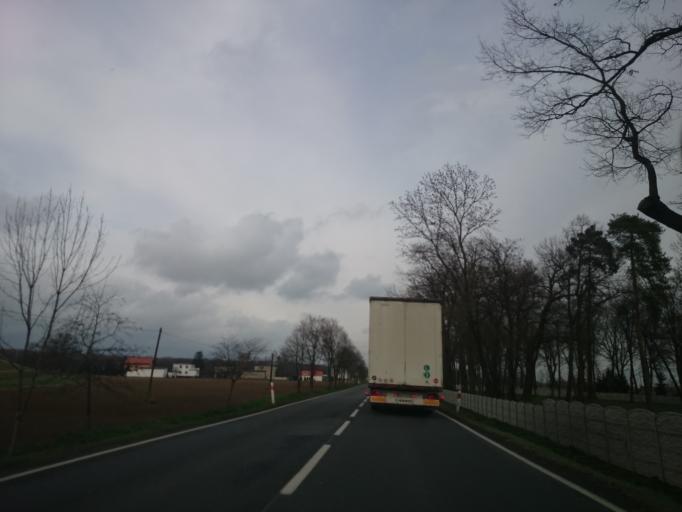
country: PL
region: Opole Voivodeship
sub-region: Powiat nyski
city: Otmuchow
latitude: 50.4517
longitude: 17.1461
